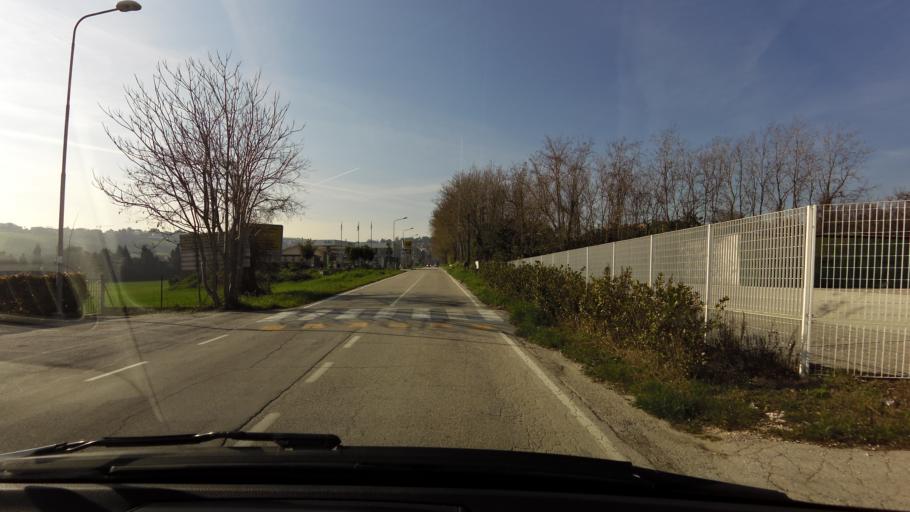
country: IT
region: The Marches
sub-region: Provincia di Ancona
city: Marcelli
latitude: 43.4977
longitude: 13.6204
